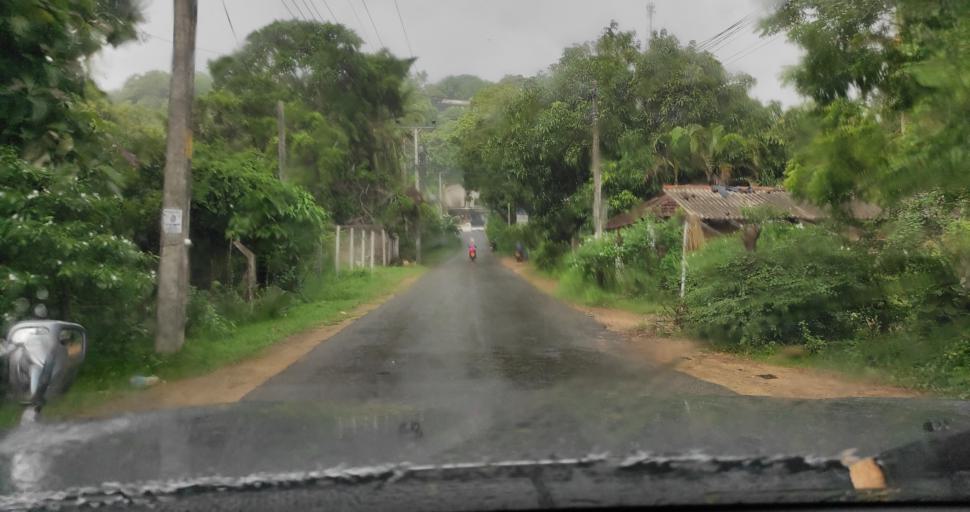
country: LK
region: Eastern Province
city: Trincomalee
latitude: 8.3681
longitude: 81.0053
